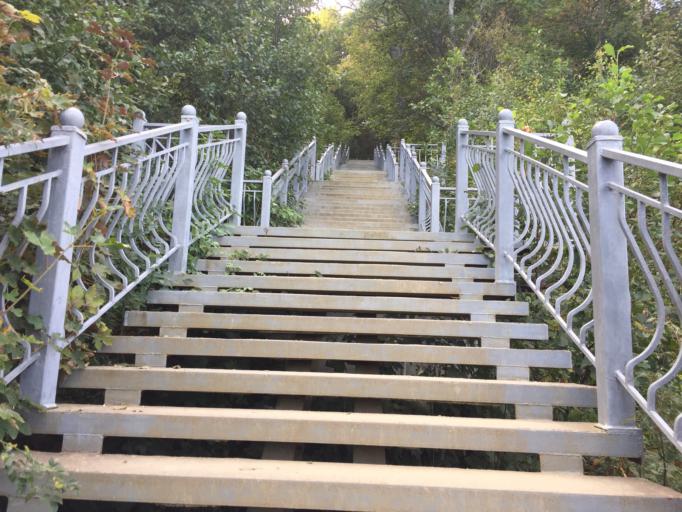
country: RU
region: Kaliningrad
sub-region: Gorod Svetlogorsk
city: Svetlogorsk
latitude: 54.9483
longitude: 20.1653
